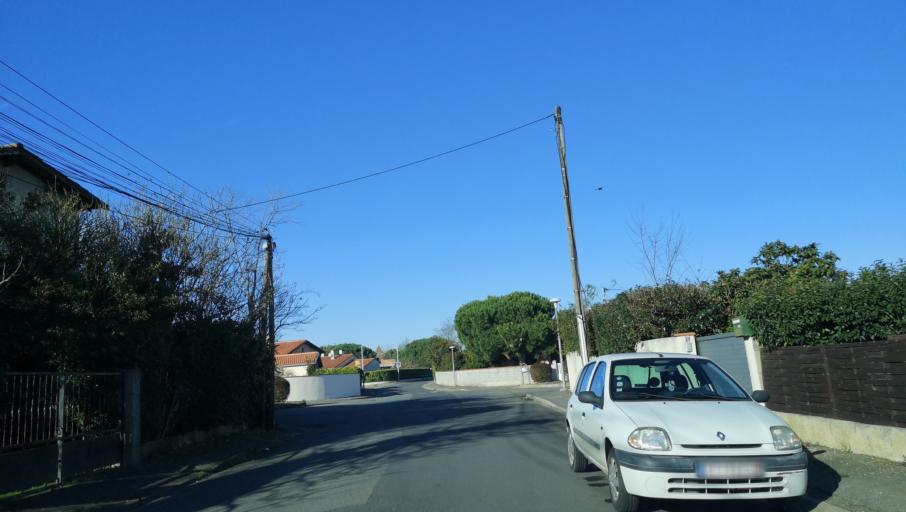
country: FR
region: Midi-Pyrenees
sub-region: Departement de la Haute-Garonne
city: Beauzelle
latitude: 43.6655
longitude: 1.3822
